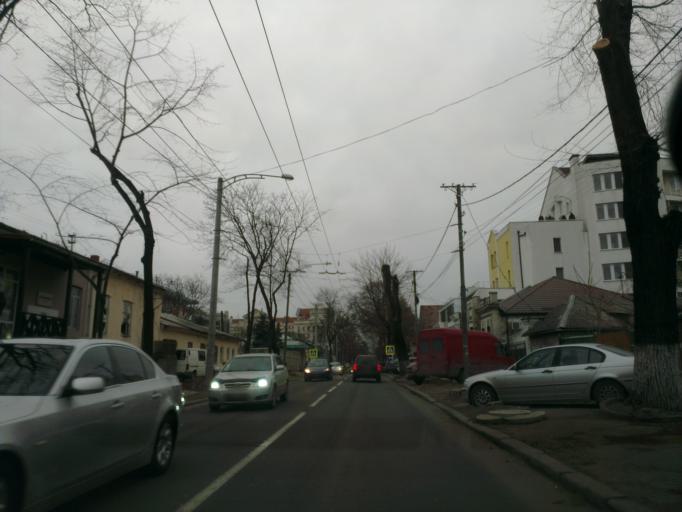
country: MD
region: Chisinau
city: Chisinau
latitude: 47.0160
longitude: 28.8258
